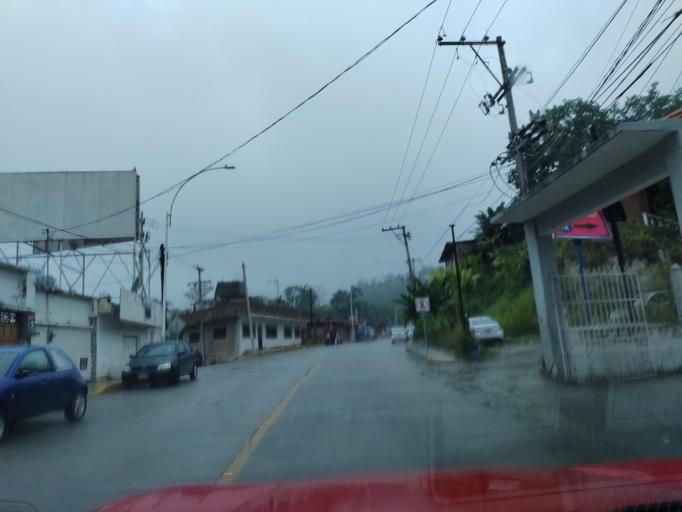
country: MX
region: Veracruz
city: Papantla de Olarte
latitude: 20.4503
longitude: -97.3295
